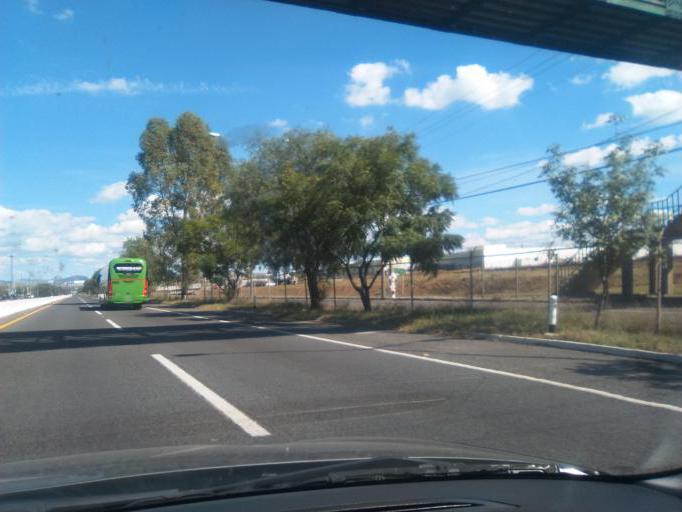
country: MX
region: Guanajuato
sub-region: Silao de la Victoria
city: Aguas Buenas
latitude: 20.9501
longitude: -101.3933
